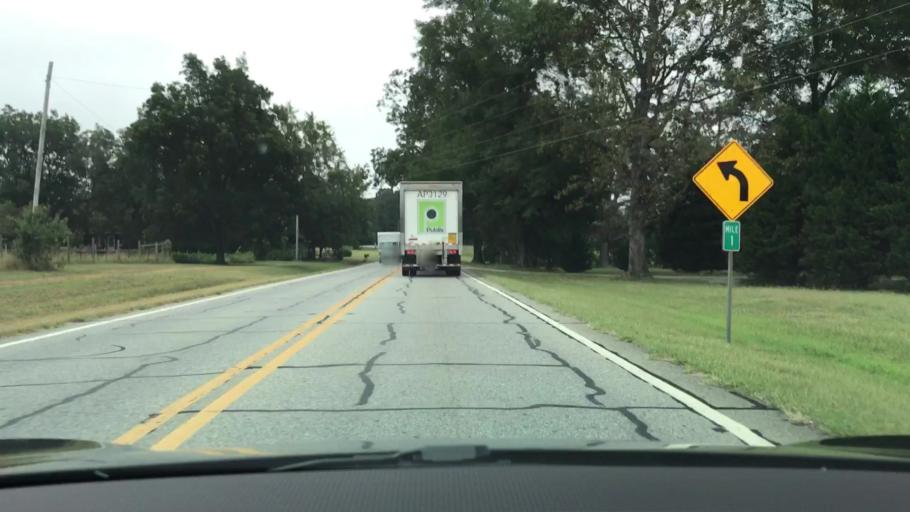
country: US
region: Georgia
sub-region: Oconee County
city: Watkinsville
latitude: 33.7446
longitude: -83.3019
